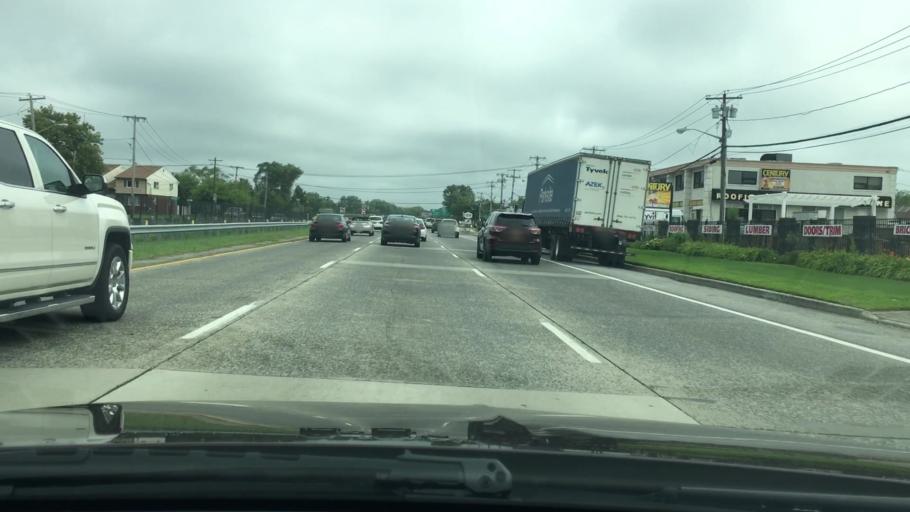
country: US
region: New York
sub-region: Suffolk County
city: North Lindenhurst
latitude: 40.7066
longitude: -73.3713
